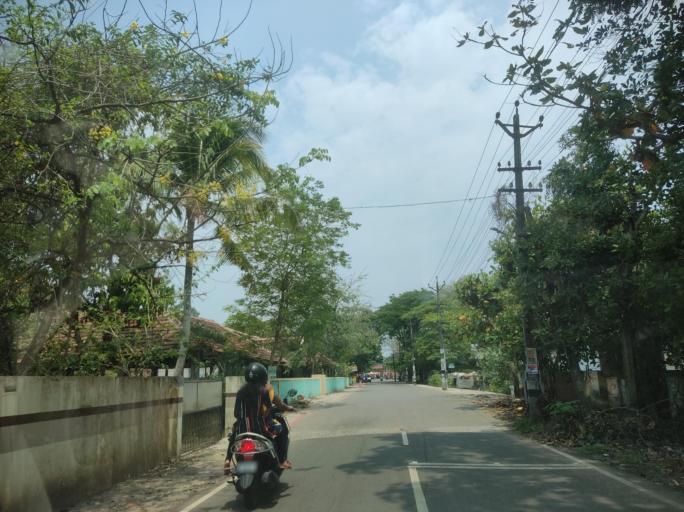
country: IN
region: Kerala
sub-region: Alappuzha
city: Vayalar
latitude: 9.7066
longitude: 76.3258
